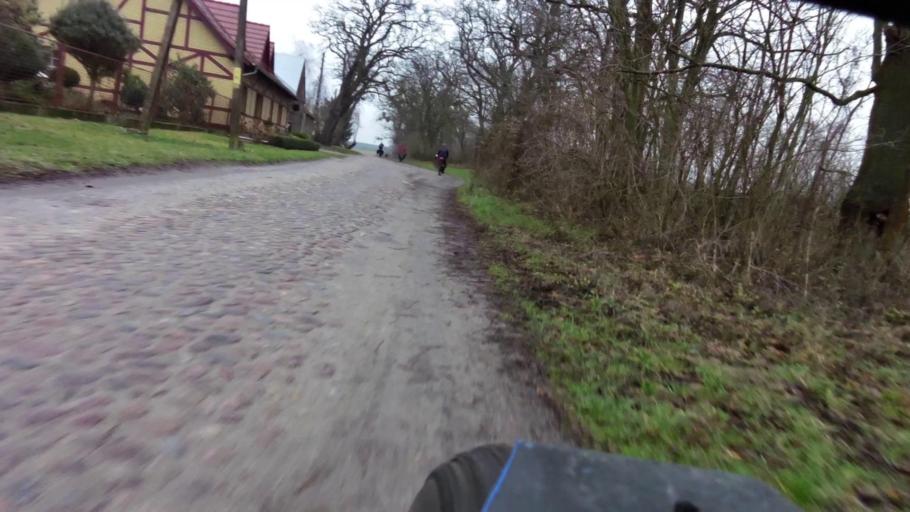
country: PL
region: Lubusz
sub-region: Powiat gorzowski
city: Witnica
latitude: 52.6787
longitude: 14.8043
